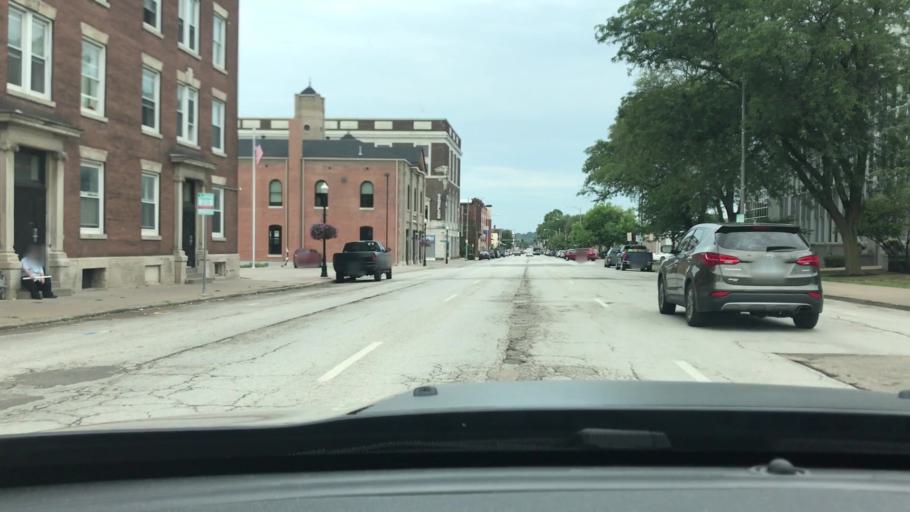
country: US
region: Iowa
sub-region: Scott County
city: Davenport
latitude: 41.5235
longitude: -90.5787
